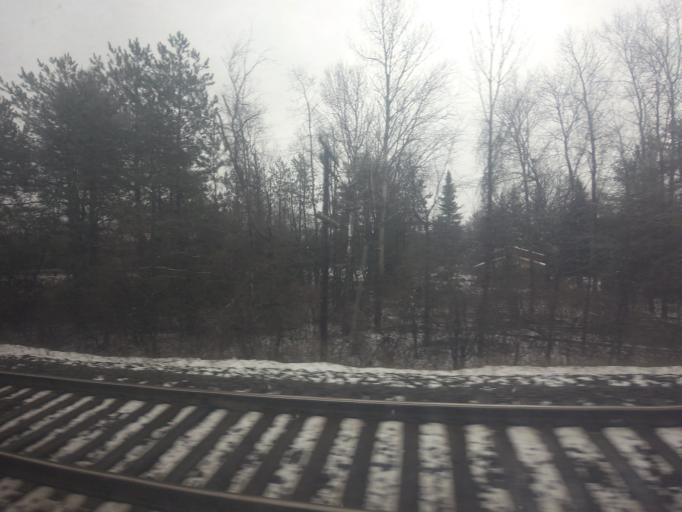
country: CA
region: Ontario
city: Quinte West
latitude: 44.1045
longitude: -77.6084
